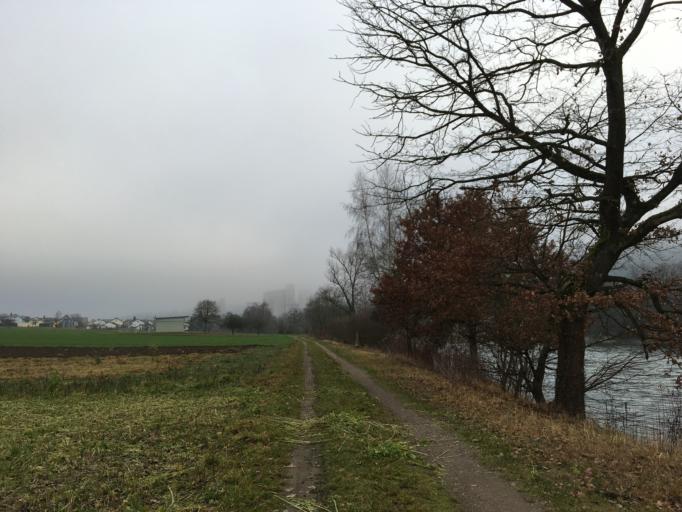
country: CH
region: Aargau
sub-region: Bezirk Zurzach
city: Bad Zurzach
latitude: 47.5745
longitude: 8.3226
